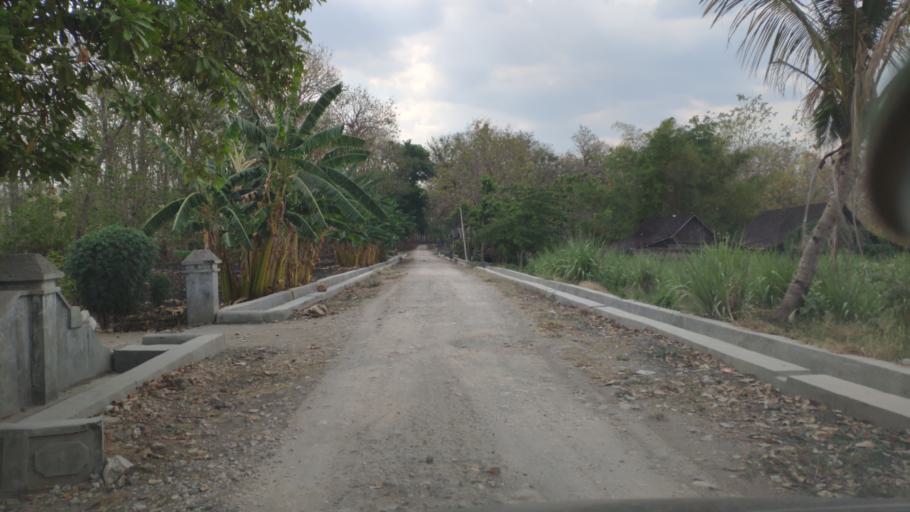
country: ID
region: Central Java
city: Randublatung
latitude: -7.3097
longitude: 111.3576
